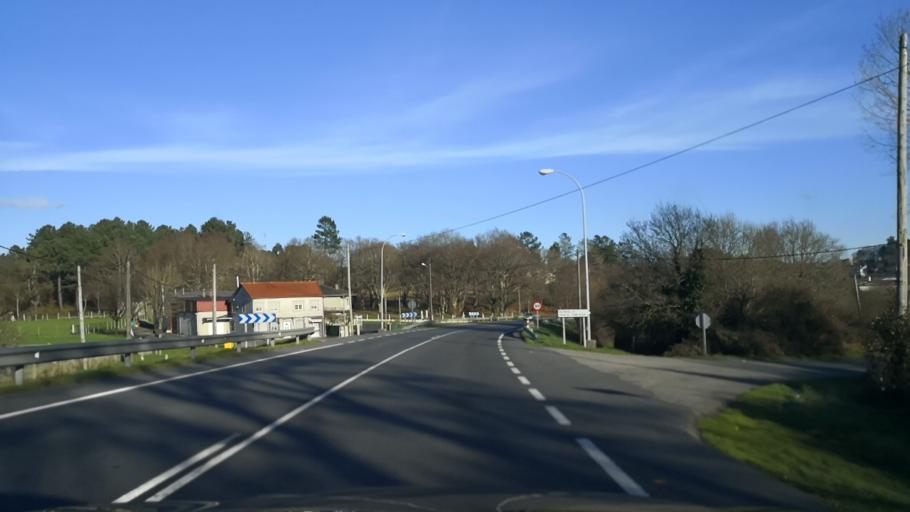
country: ES
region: Galicia
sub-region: Provincia de Pontevedra
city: Silleda
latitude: 42.6870
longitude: -8.2063
